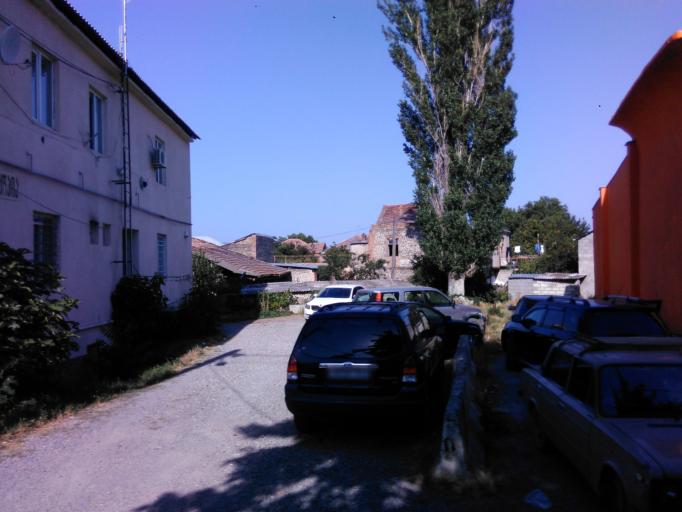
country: GE
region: Shida Kartli
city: Kaspi
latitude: 41.9322
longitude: 44.5742
